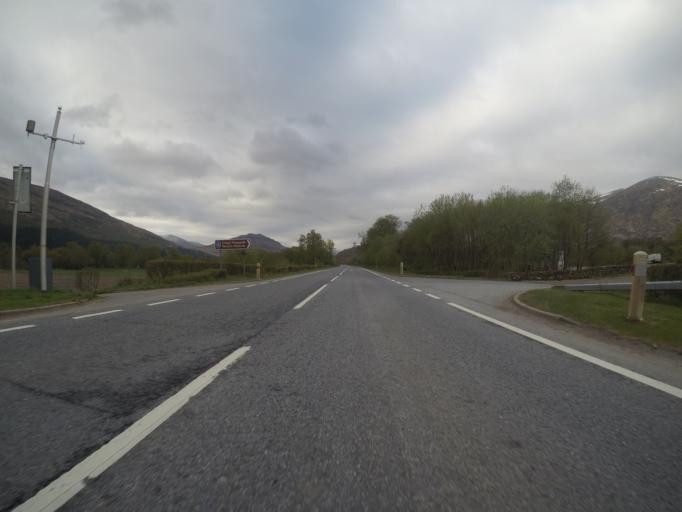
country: GB
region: Scotland
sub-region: Highland
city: Spean Bridge
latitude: 56.9515
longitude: -4.4953
